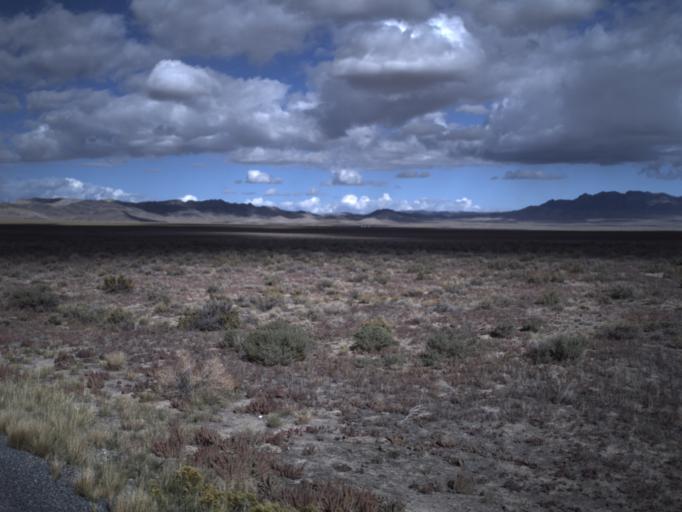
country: US
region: Utah
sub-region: Beaver County
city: Milford
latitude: 38.5462
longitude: -113.7193
